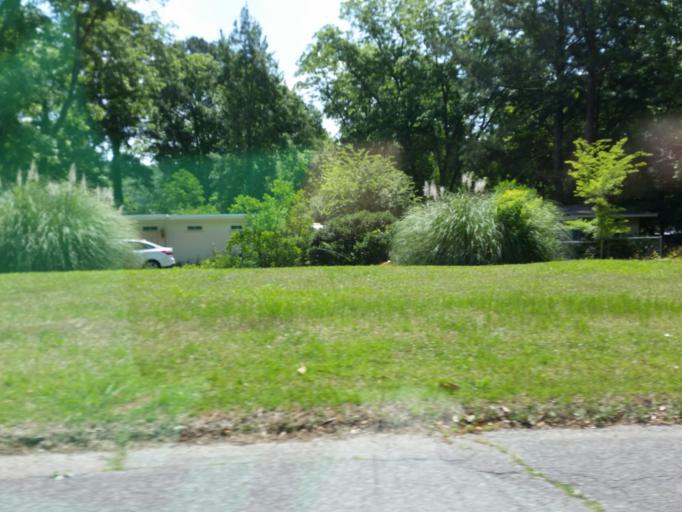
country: US
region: Mississippi
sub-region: Lauderdale County
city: Meridian
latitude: 32.3898
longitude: -88.7163
